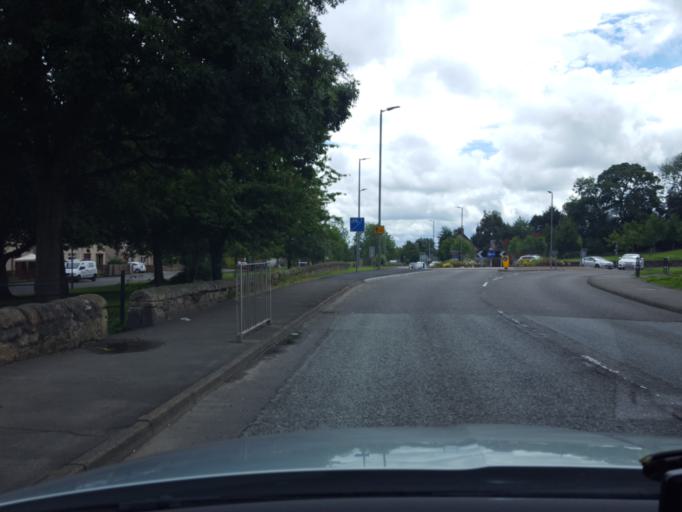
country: GB
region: Scotland
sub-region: Stirling
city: Plean
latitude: 56.0638
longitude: -3.8741
